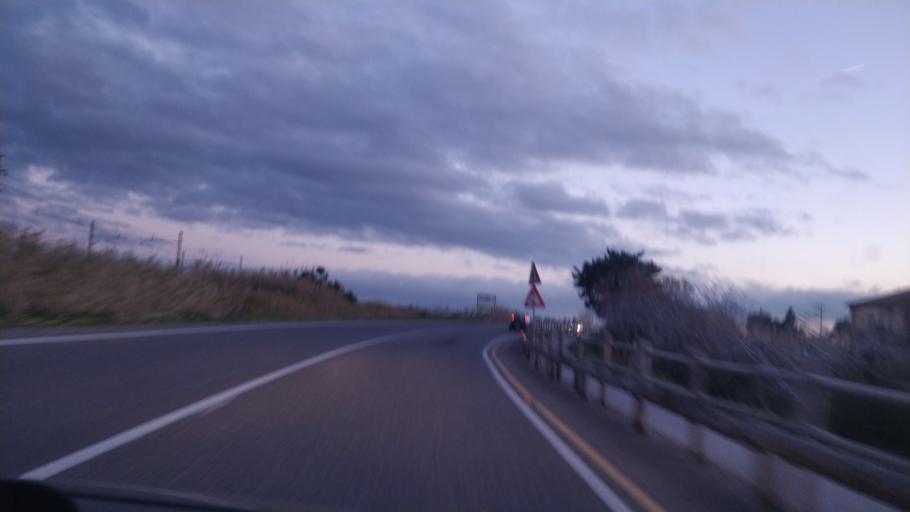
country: IT
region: Tuscany
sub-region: Provincia di Livorno
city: Vada
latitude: 43.3730
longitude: 10.4497
